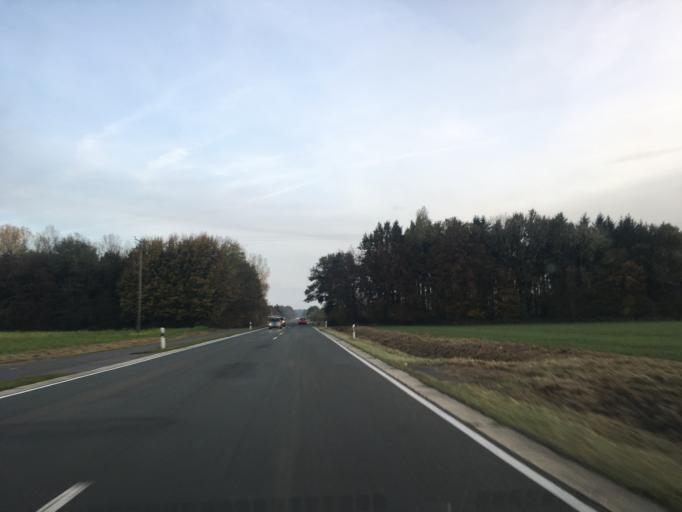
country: DE
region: North Rhine-Westphalia
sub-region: Regierungsbezirk Munster
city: Altenberge
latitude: 52.0880
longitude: 7.4222
